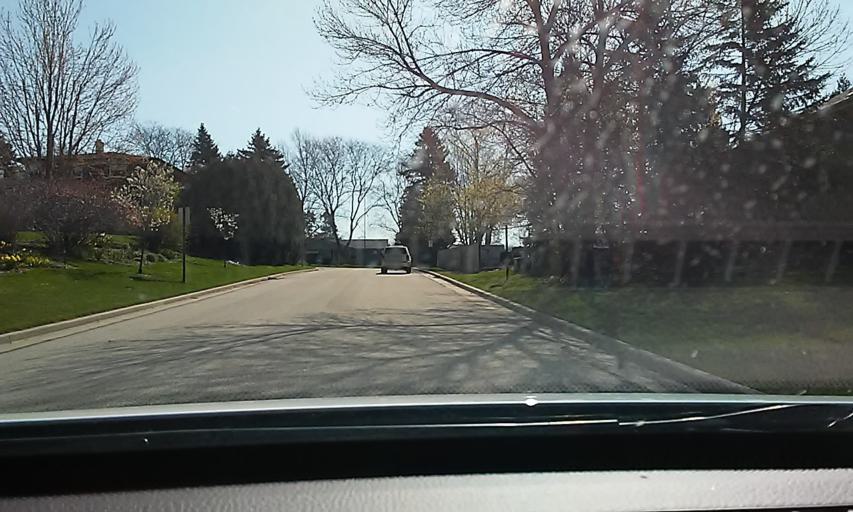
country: US
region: Wisconsin
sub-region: Milwaukee County
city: Hales Corners
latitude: 42.9787
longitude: -88.0503
